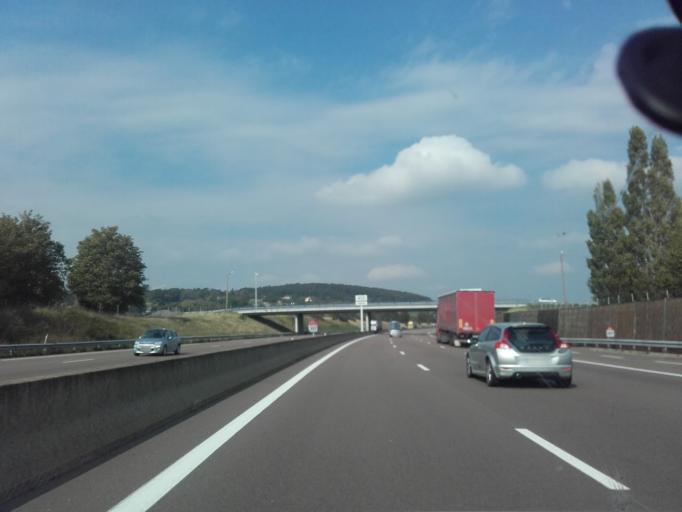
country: FR
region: Bourgogne
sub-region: Departement de Saone-et-Loire
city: Tournus
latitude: 46.5664
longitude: 4.8957
